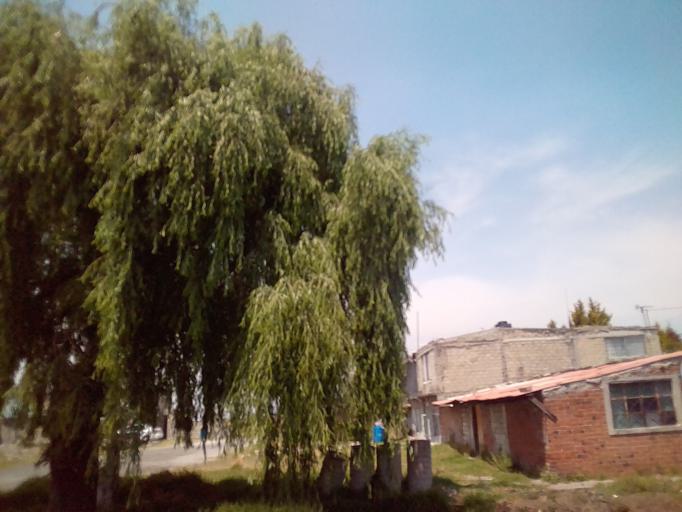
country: MX
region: Mexico
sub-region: Toluca
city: Guadalupe Totoltepec
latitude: 19.3495
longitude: -99.5581
